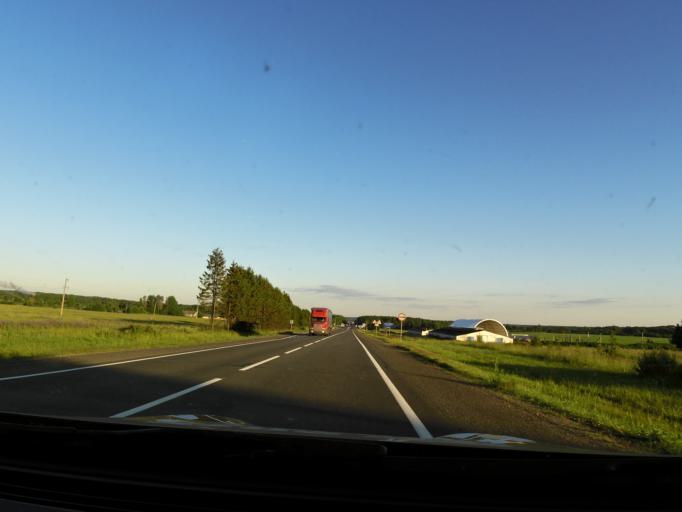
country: RU
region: Vologda
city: Gryazovets
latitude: 58.7722
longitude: 40.2759
